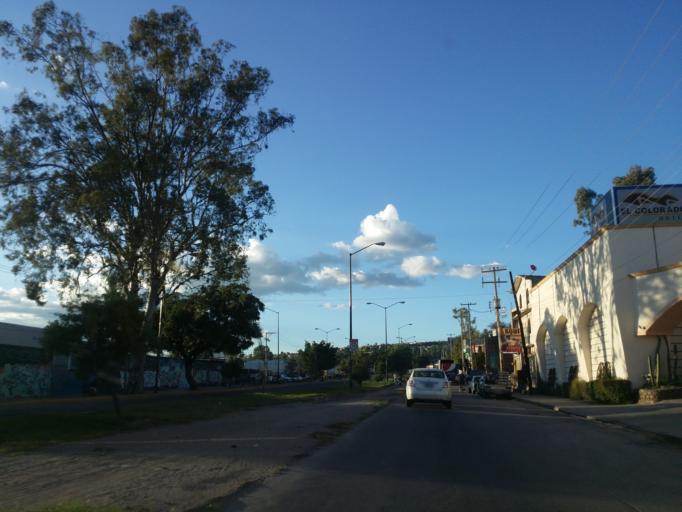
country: MX
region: Guanajuato
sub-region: Leon
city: Medina
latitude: 21.1926
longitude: -101.6657
